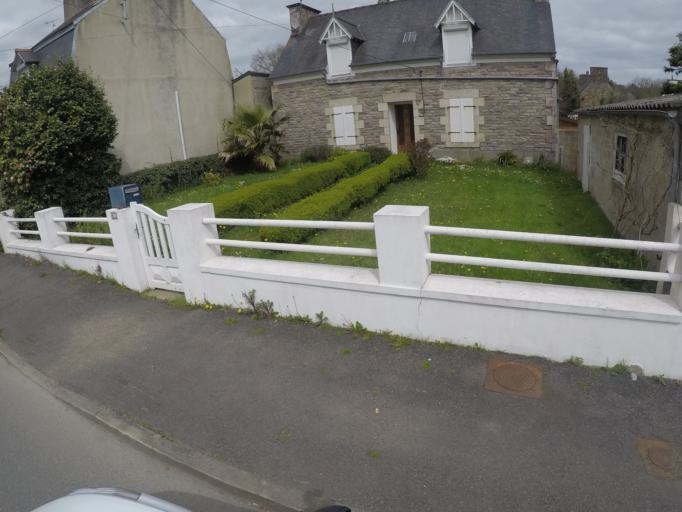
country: FR
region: Brittany
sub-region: Departement des Cotes-d'Armor
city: Plouha
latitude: 48.6724
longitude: -2.9258
